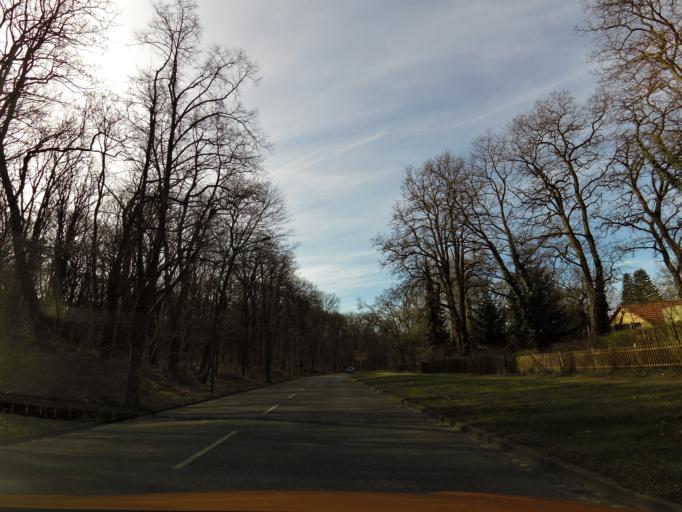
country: DE
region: Brandenburg
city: Potsdam
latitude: 52.3832
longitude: 13.0567
